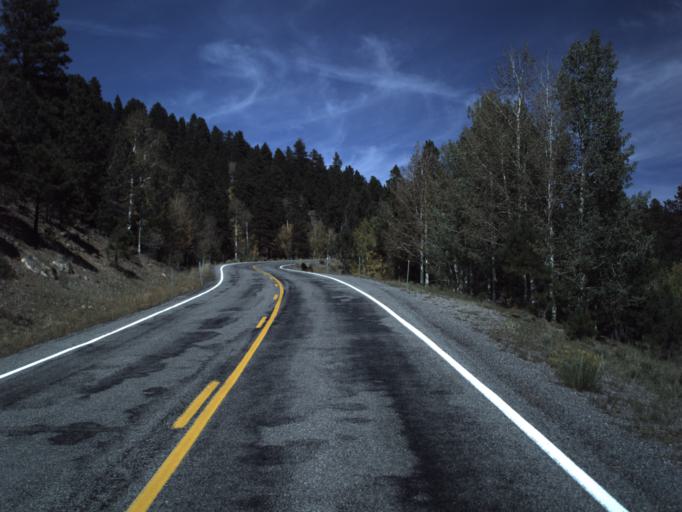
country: US
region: Utah
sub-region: Wayne County
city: Loa
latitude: 38.1383
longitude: -111.3291
